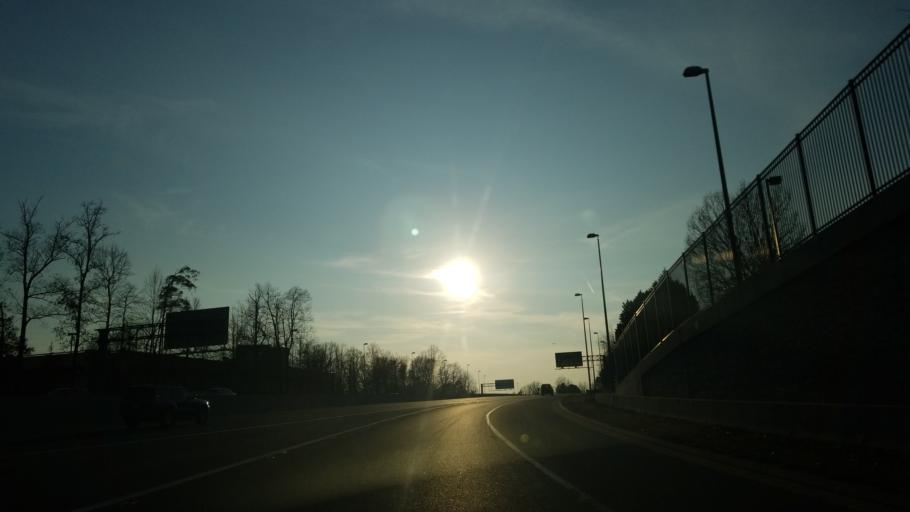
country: US
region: Virginia
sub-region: Fairfax County
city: Greenbriar
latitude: 38.8612
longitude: -77.3842
